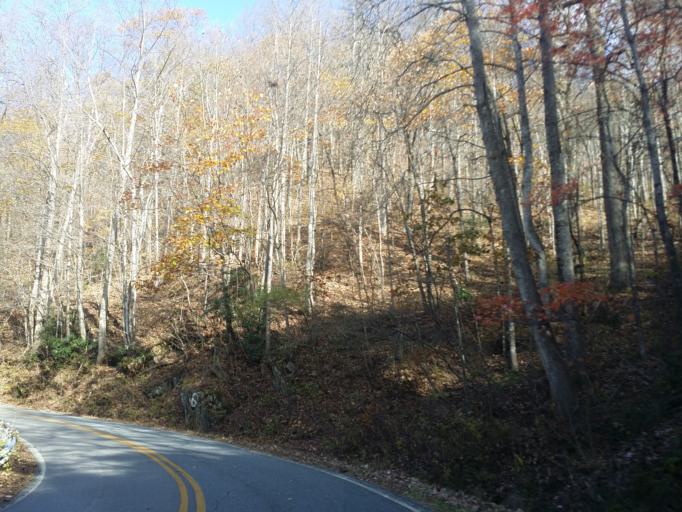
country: US
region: North Carolina
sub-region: McDowell County
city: Marion
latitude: 35.7585
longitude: -82.1549
